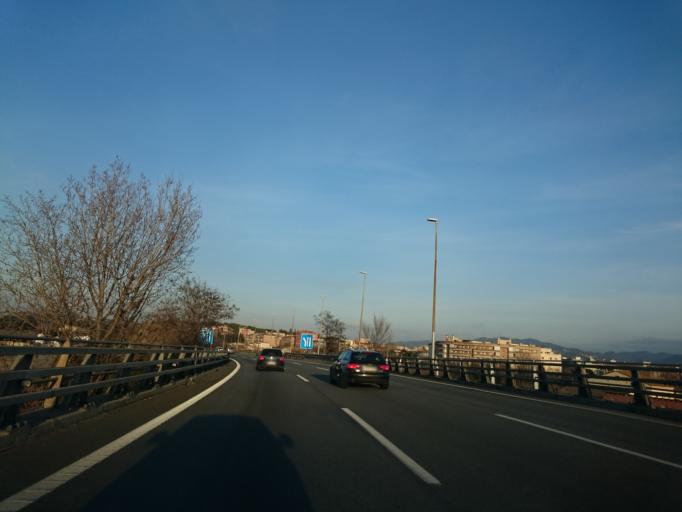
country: ES
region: Catalonia
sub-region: Provincia de Barcelona
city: Montmelo
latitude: 41.5494
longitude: 2.2360
